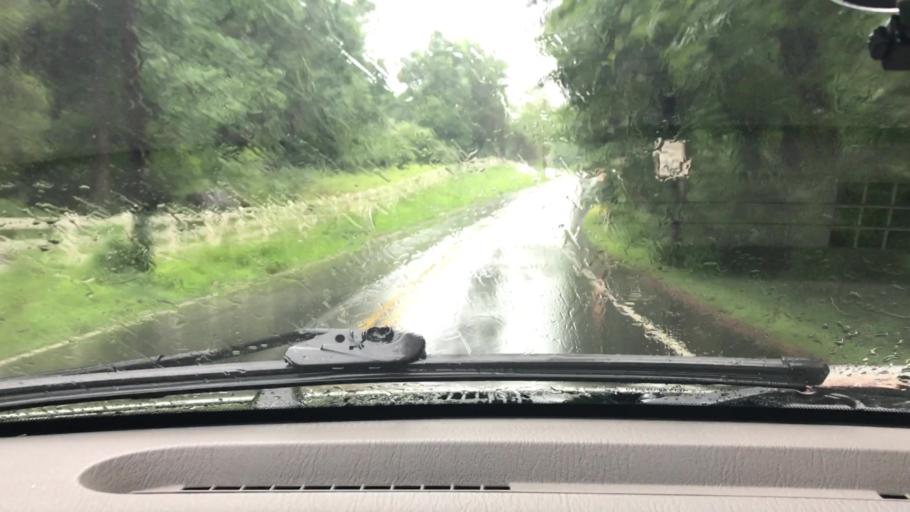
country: US
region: Pennsylvania
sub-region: Lancaster County
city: Elizabethtown
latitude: 40.1538
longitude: -76.6288
